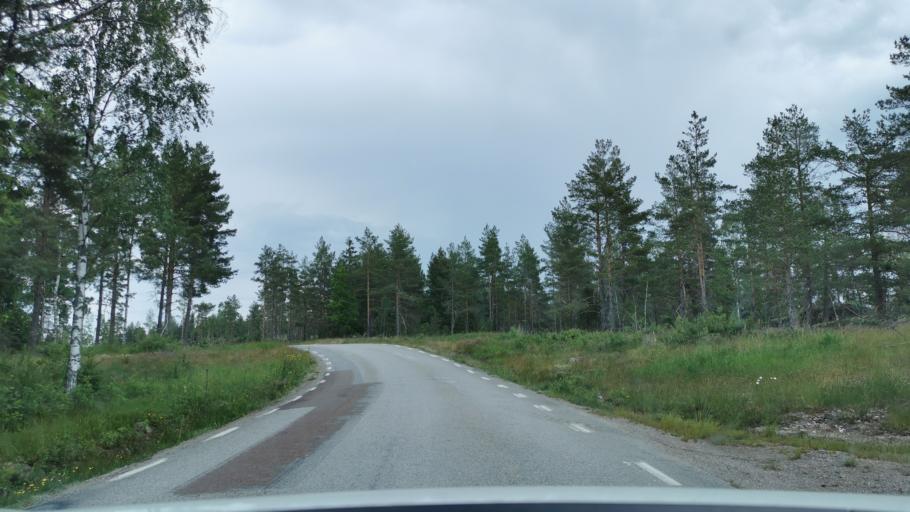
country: SE
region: Vaestra Goetaland
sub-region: Bengtsfors Kommun
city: Dals Langed
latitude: 58.8787
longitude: 12.4047
